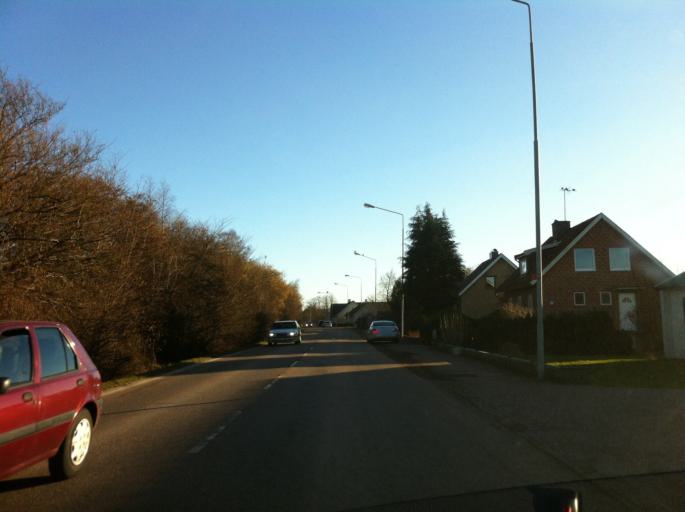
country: SE
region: Skane
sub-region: Helsingborg
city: Morarp
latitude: 56.0672
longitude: 12.8681
